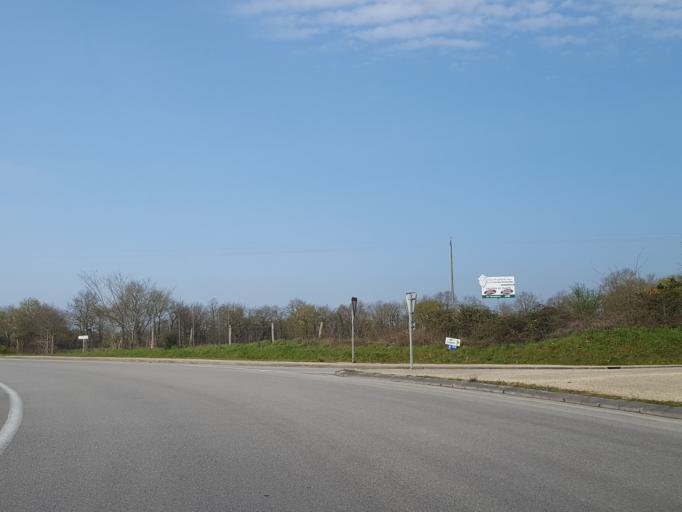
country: FR
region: Pays de la Loire
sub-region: Departement de la Vendee
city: La Roche-sur-Yon
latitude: 46.6659
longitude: -1.4655
